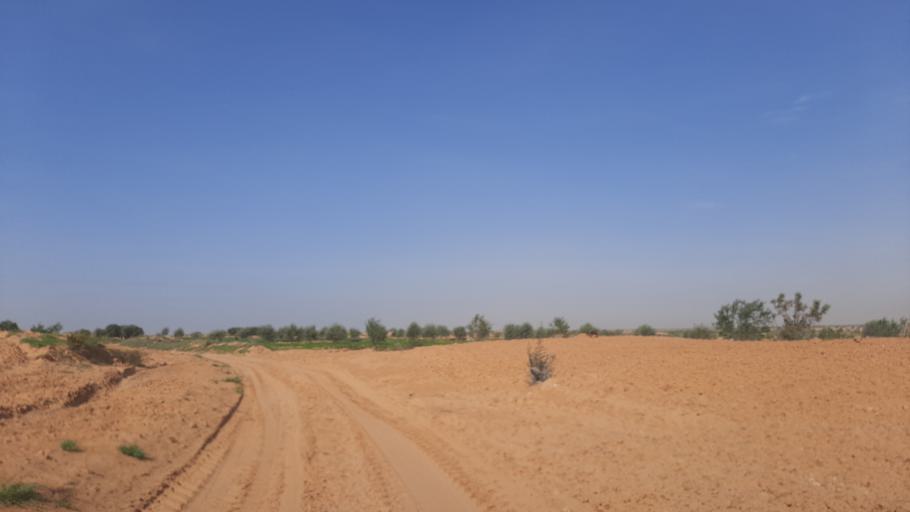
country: TN
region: Madanin
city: Zarzis
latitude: 33.4347
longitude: 10.8088
